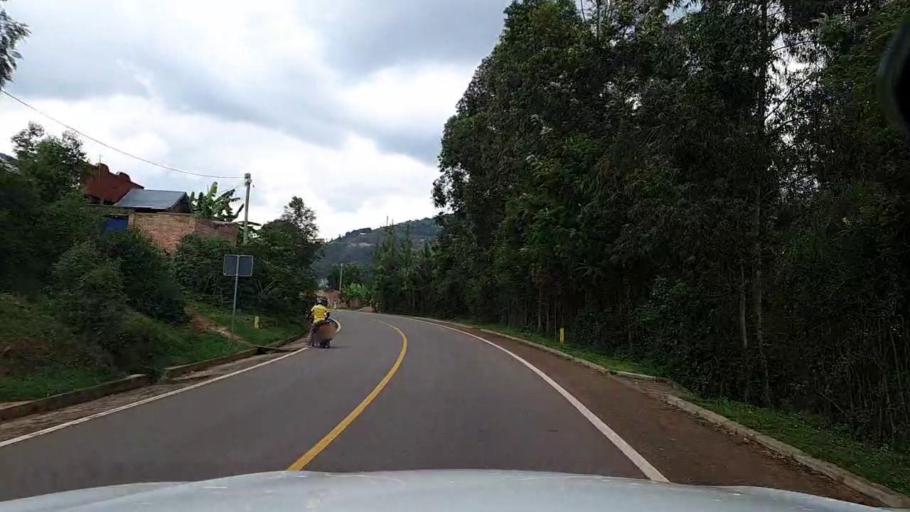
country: RW
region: Northern Province
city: Byumba
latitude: -1.6780
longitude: 30.0998
